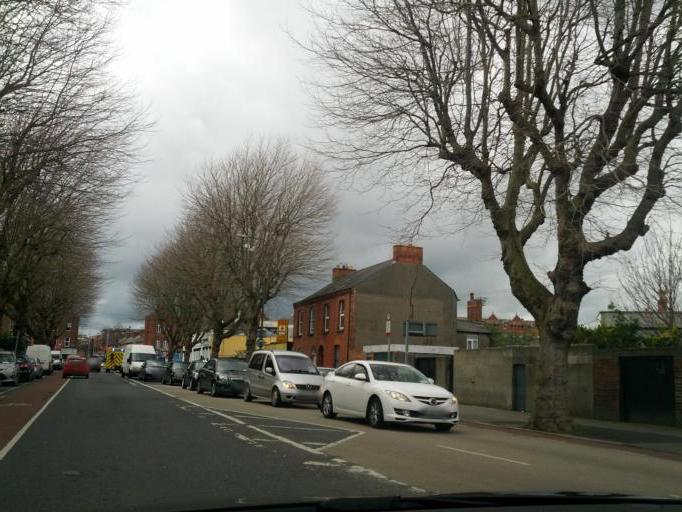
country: IE
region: Leinster
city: Drumcondra
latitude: 53.3593
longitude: -6.2594
